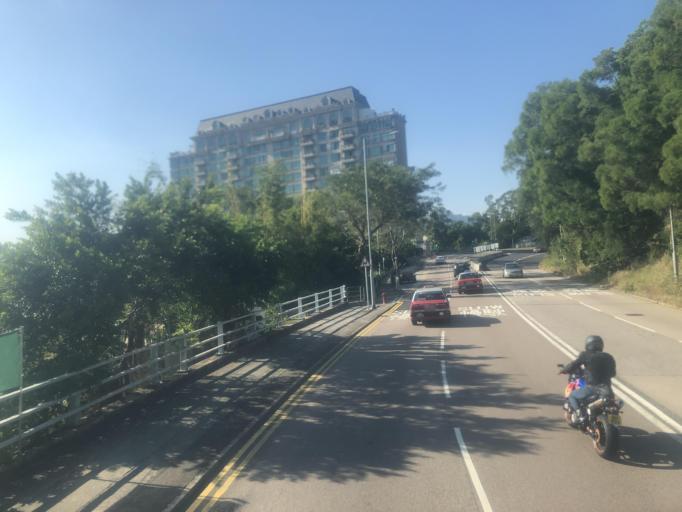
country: HK
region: Sham Shui Po
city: Sham Shui Po
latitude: 22.3438
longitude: 114.1518
